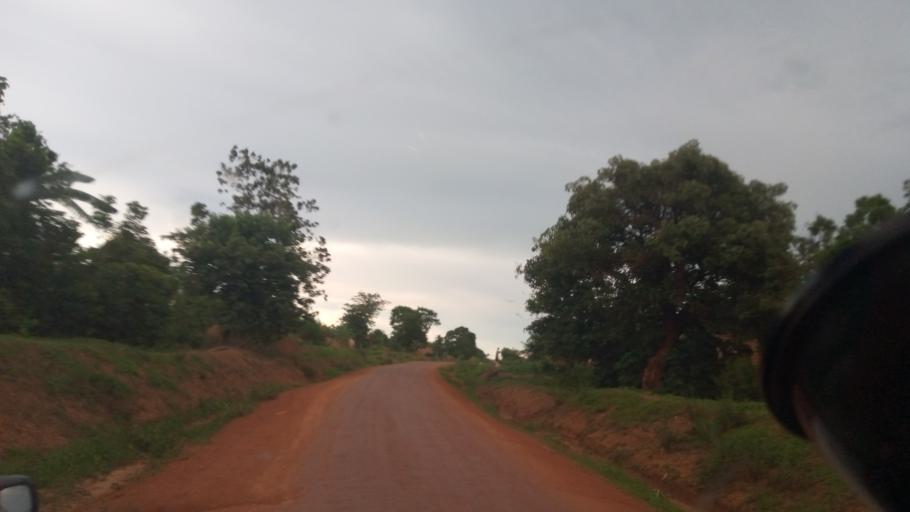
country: UG
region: Northern Region
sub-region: Kole District
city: Kole
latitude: 2.4654
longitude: 32.9364
